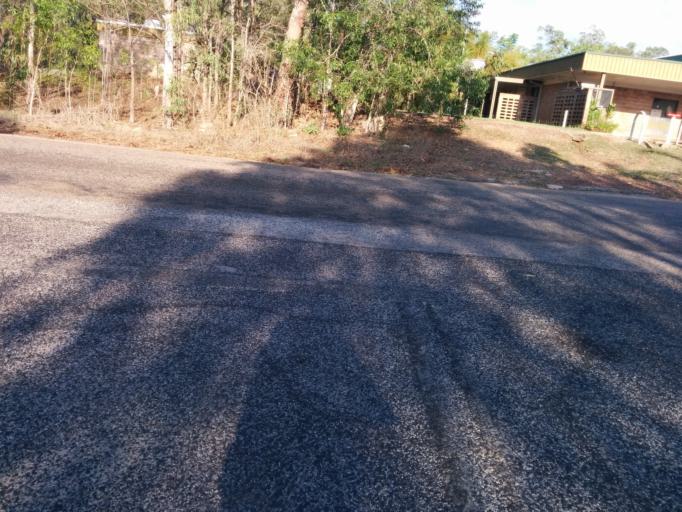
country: AU
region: Northern Territory
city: Alyangula
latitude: -13.8479
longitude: 136.4208
